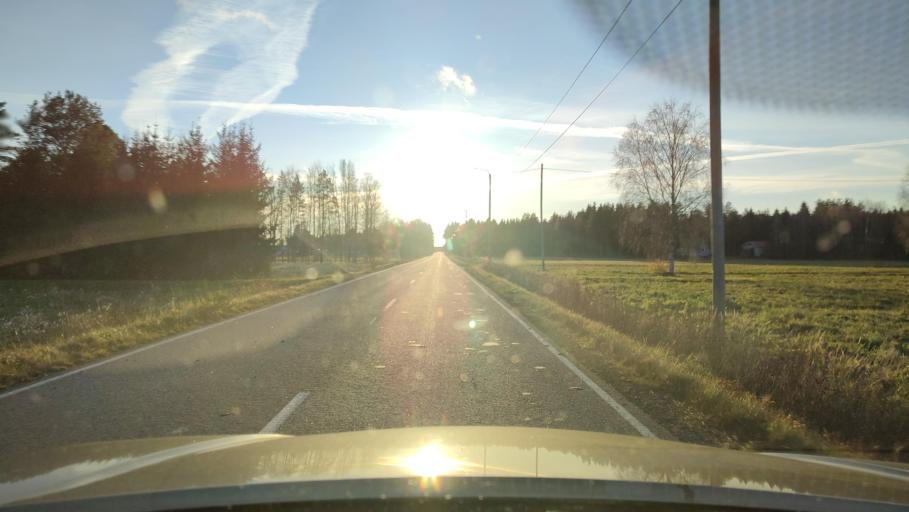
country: FI
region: Ostrobothnia
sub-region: Vaasa
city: Malax
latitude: 62.7010
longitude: 21.5840
